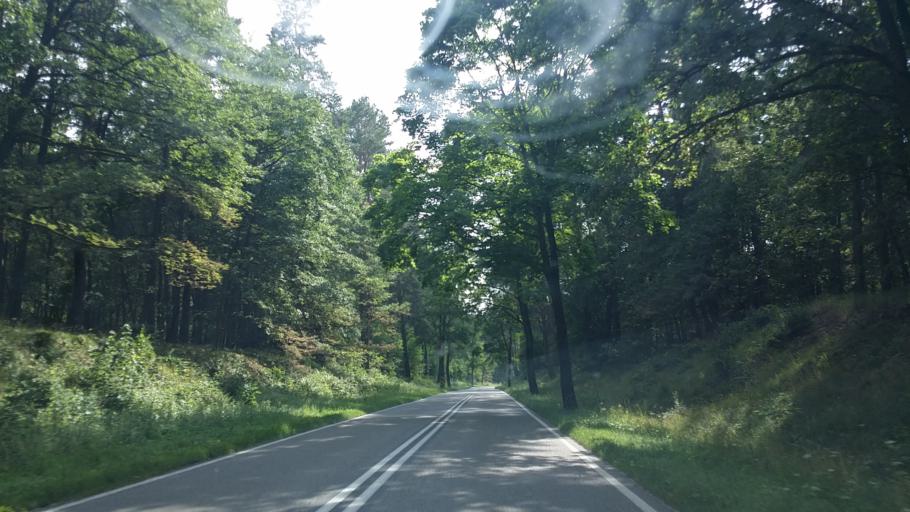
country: PL
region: West Pomeranian Voivodeship
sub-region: Powiat mysliborski
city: Barlinek
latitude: 53.0048
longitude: 15.2496
